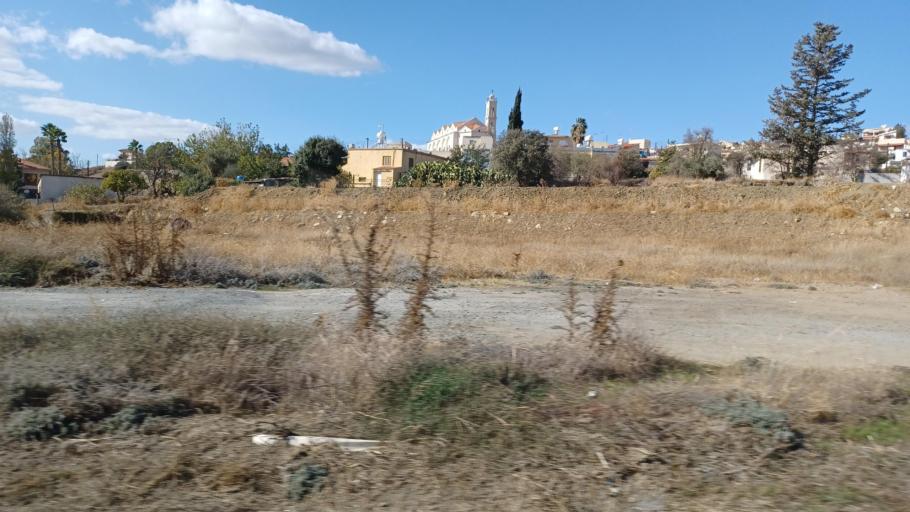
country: CY
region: Limassol
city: Pyrgos
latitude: 34.7474
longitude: 33.2143
